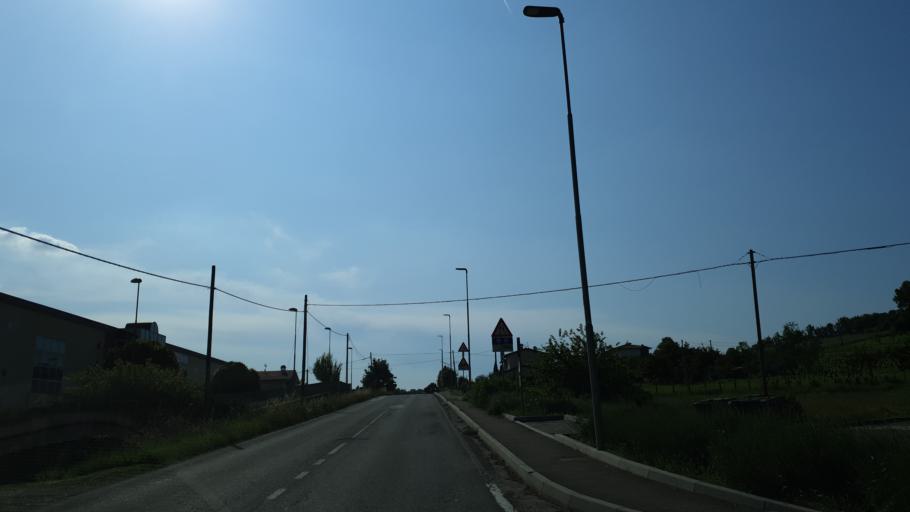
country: IT
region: Tuscany
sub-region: Province of Arezzo
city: Soci
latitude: 43.7380
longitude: 11.8057
